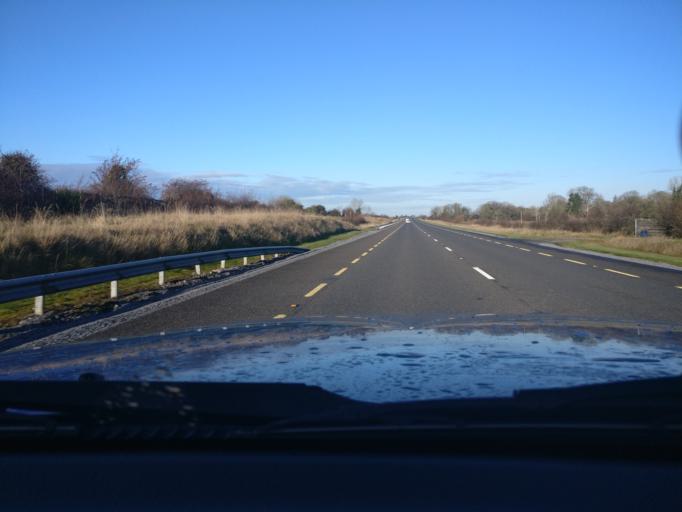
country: IE
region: Connaught
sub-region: County Galway
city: Loughrea
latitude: 53.2234
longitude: -8.5853
